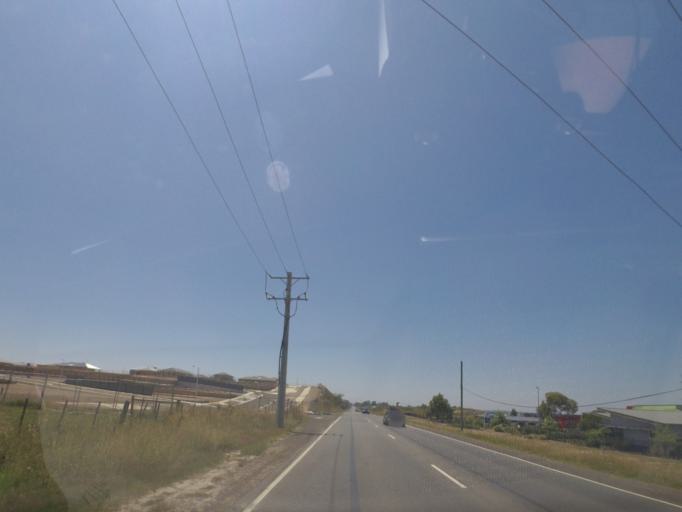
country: AU
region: Victoria
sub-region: Whittlesea
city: Mernda
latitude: -37.5980
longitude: 145.0739
